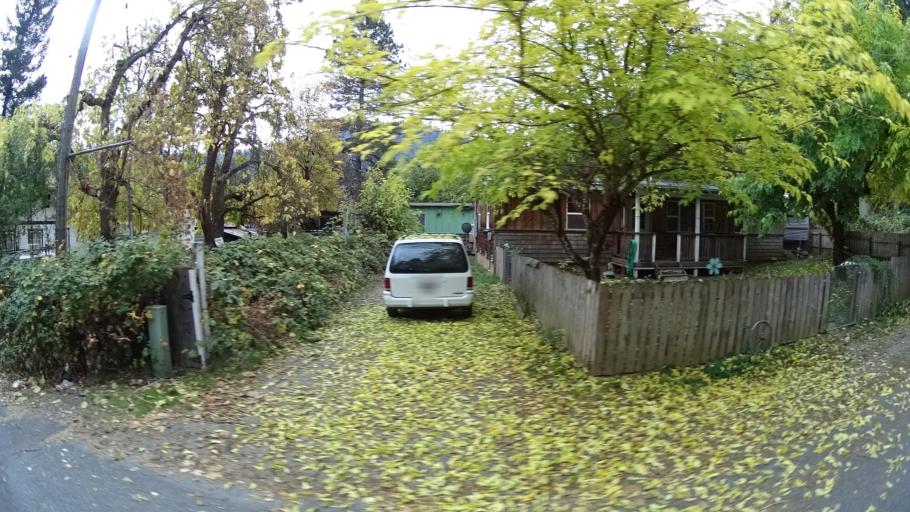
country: US
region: California
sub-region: Siskiyou County
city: Happy Camp
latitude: 41.8006
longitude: -123.3811
